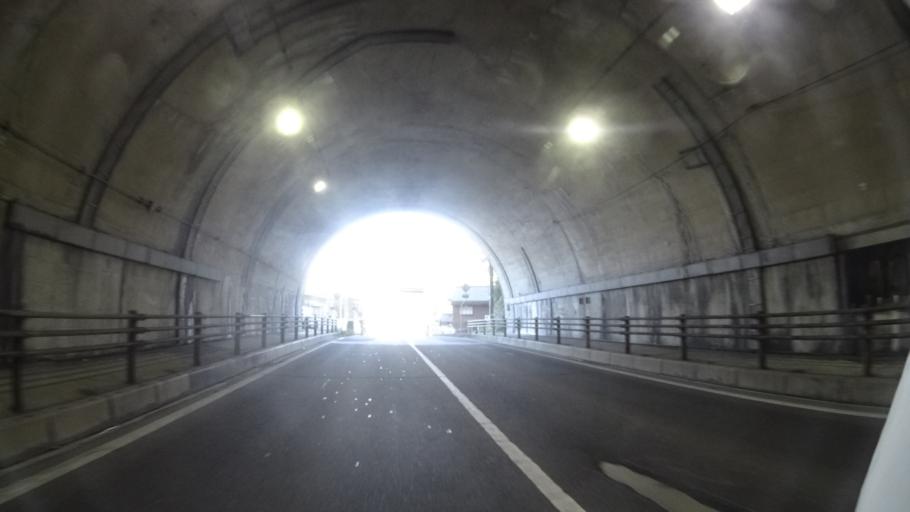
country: JP
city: Asahi
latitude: 35.9444
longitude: 135.9877
